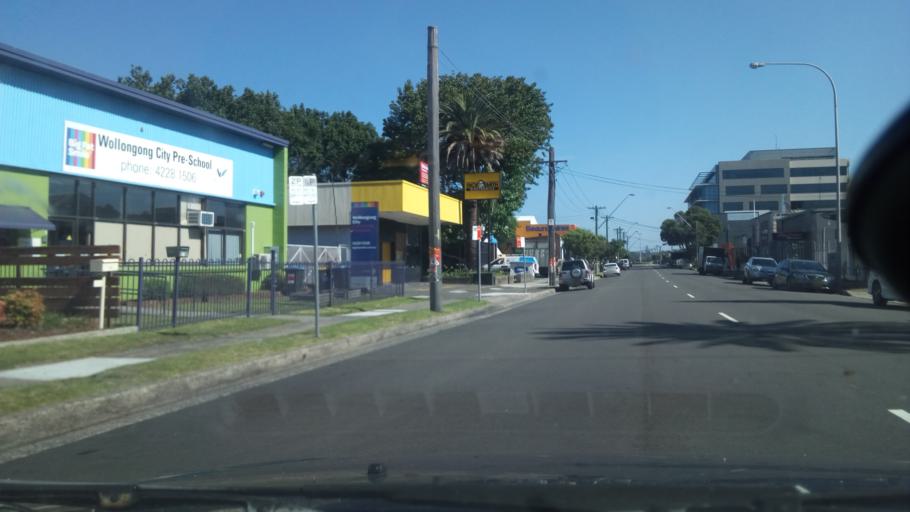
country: AU
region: New South Wales
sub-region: Wollongong
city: Wollongong
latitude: -34.4272
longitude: 150.8930
